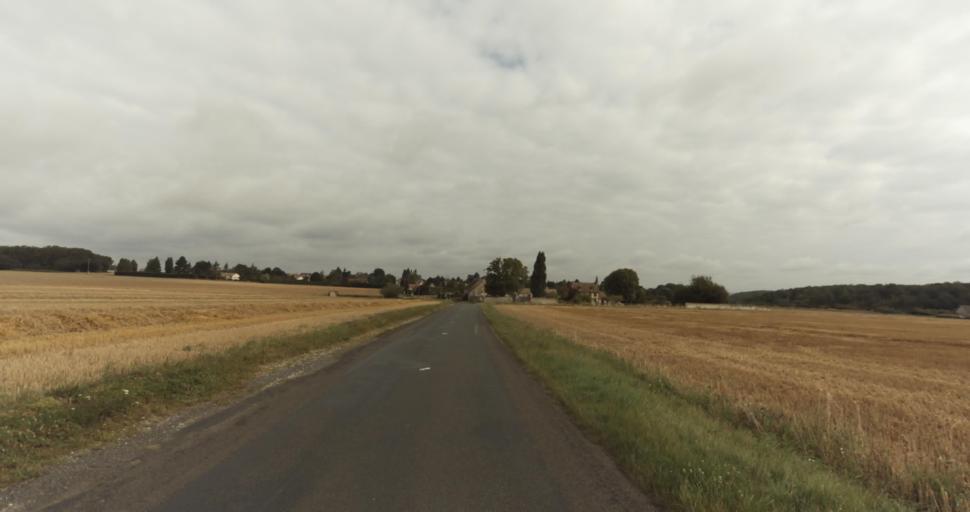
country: FR
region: Haute-Normandie
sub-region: Departement de l'Eure
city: La Couture-Boussey
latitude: 48.9075
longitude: 1.4077
